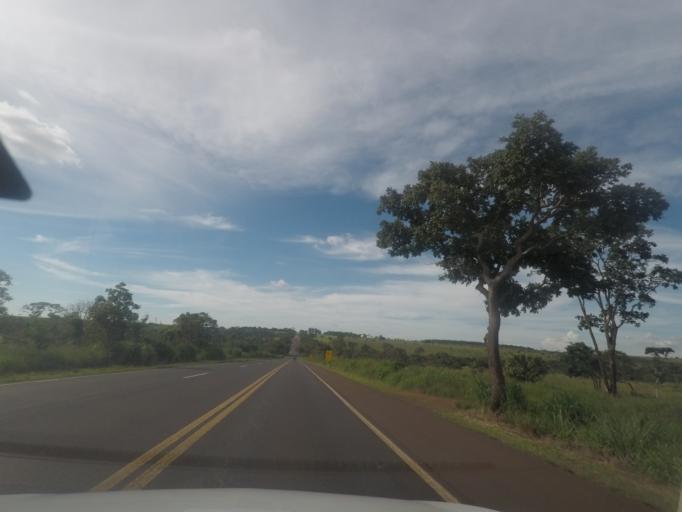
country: BR
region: Minas Gerais
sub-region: Monte Alegre De Minas
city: Monte Alegre de Minas
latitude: -18.9964
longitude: -49.0203
